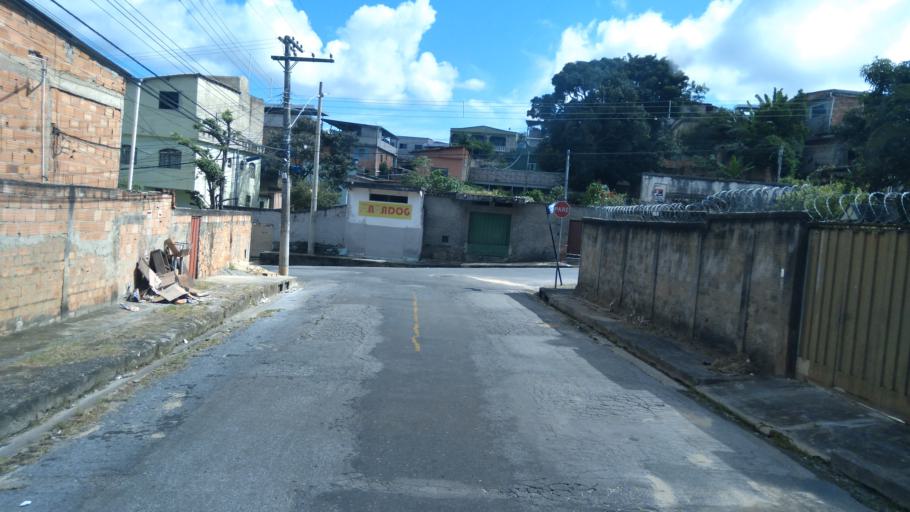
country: BR
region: Minas Gerais
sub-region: Belo Horizonte
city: Belo Horizonte
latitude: -19.8618
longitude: -43.9018
